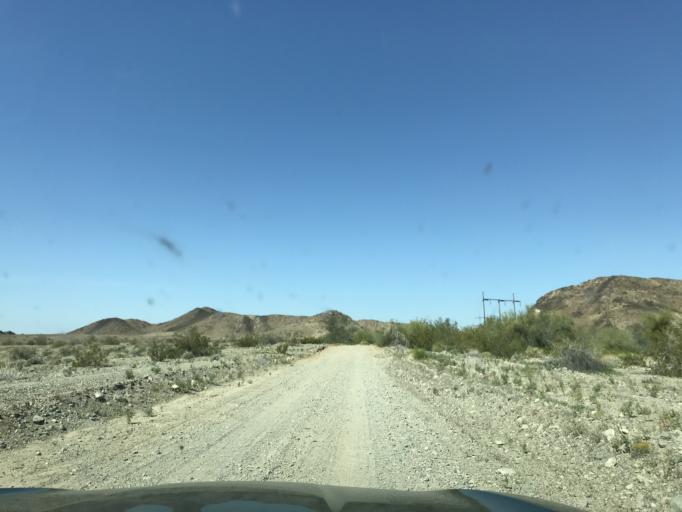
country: US
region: California
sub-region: Riverside County
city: Mesa Verde
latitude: 33.4902
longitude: -114.7852
